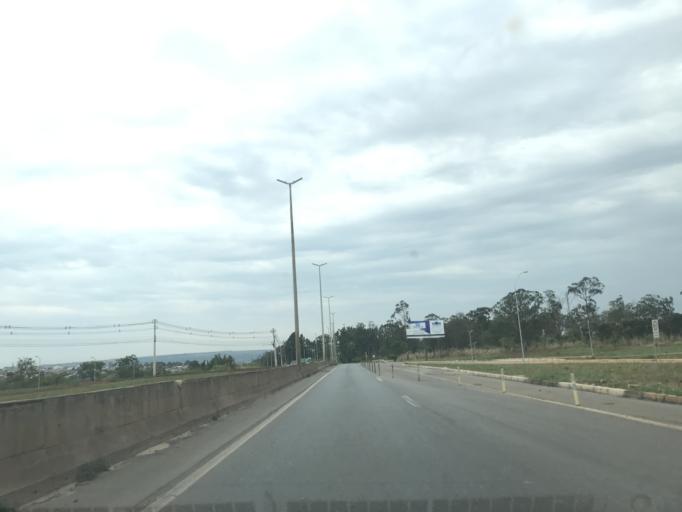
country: BR
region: Federal District
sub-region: Brasilia
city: Brasilia
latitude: -15.6860
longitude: -47.8568
